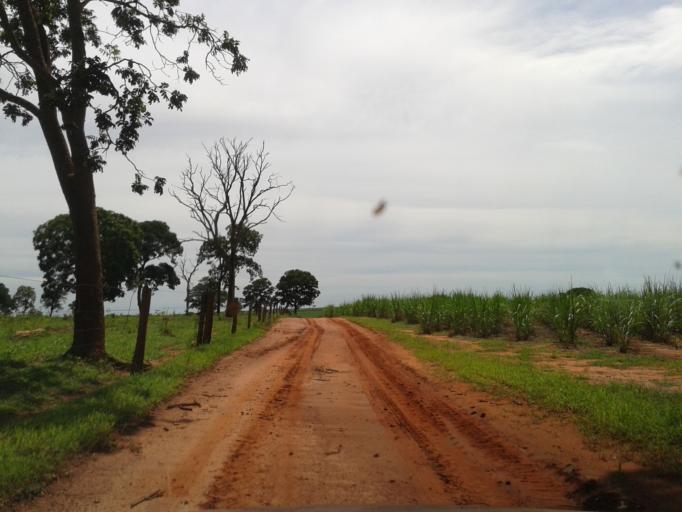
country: BR
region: Minas Gerais
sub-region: Santa Vitoria
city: Santa Vitoria
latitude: -19.2077
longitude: -50.6435
